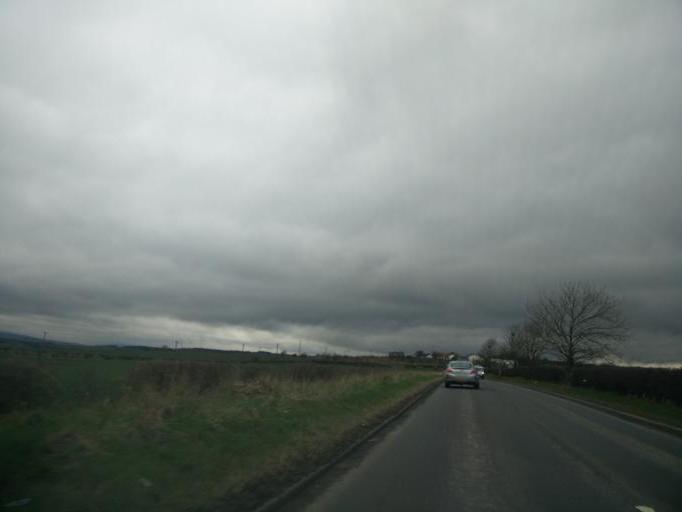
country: GB
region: England
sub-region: County Durham
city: Crook
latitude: 54.7293
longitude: -1.7306
